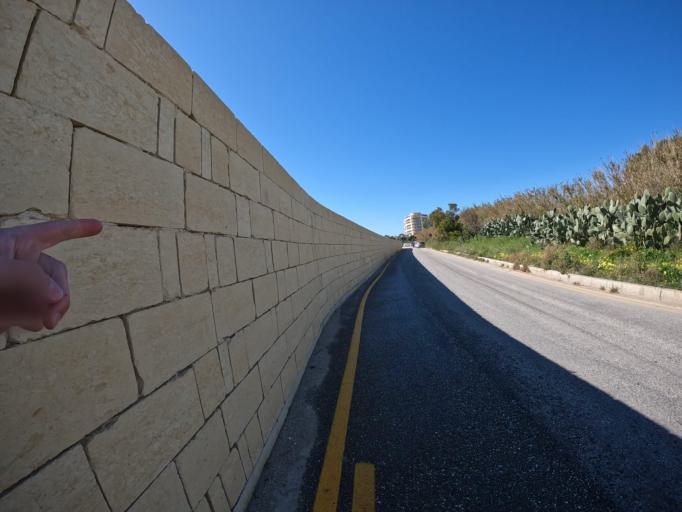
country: MT
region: L-Imgarr
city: Imgarr
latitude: 35.9355
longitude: 14.3484
